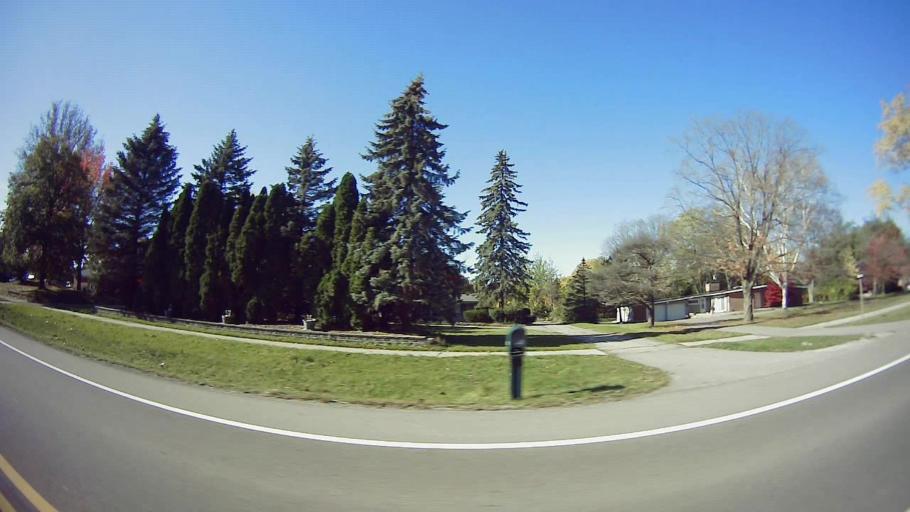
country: US
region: Michigan
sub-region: Oakland County
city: Farmington Hills
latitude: 42.4827
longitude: -83.3773
